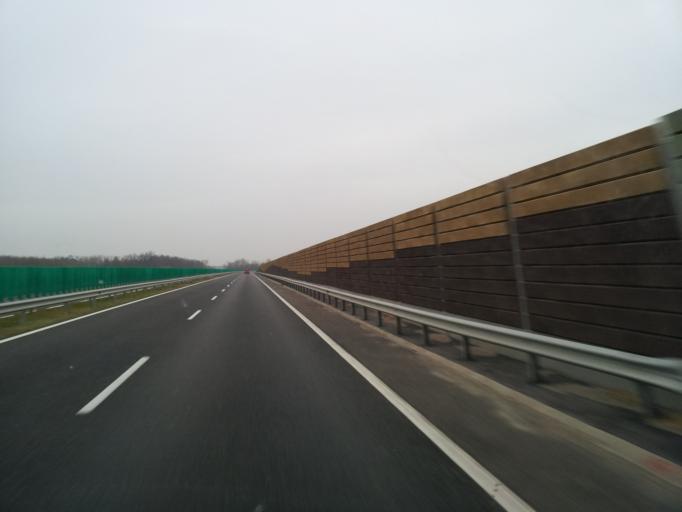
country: HU
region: Fejer
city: Sarszentmihaly
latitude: 47.1589
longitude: 18.3786
